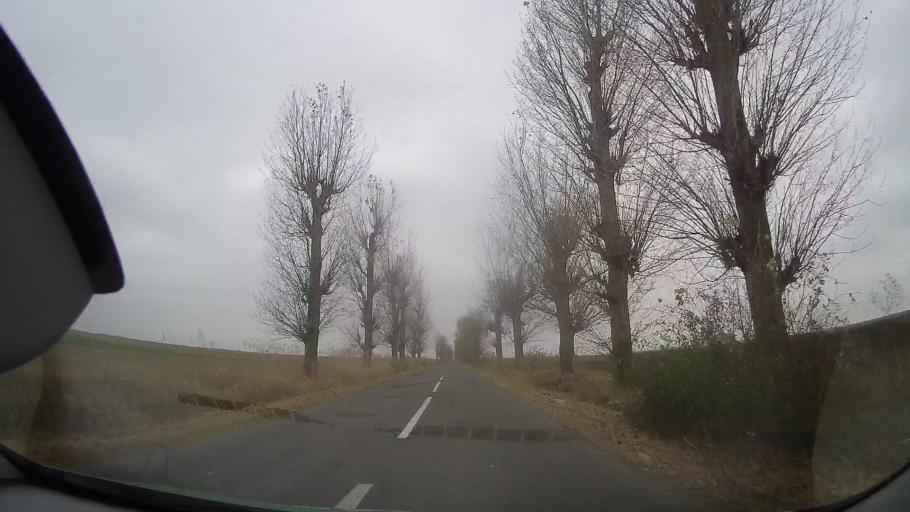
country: RO
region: Ialomita
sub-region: Comuna Grindu
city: Grindu
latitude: 44.7731
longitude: 26.8864
